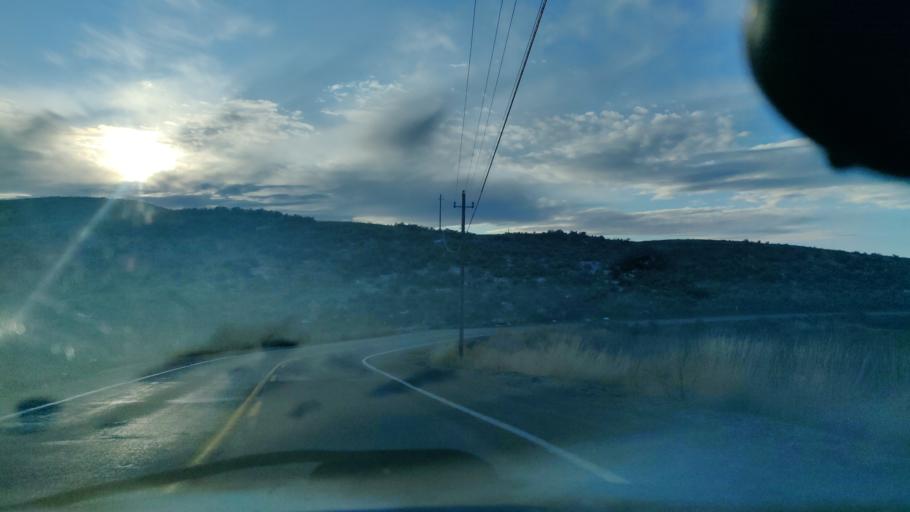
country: US
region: Idaho
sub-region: Ada County
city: Eagle
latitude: 43.7292
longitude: -116.2814
